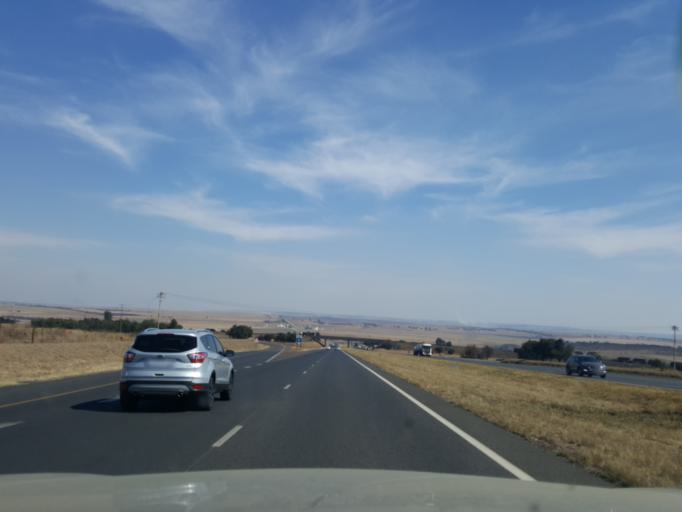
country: ZA
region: Mpumalanga
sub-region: Nkangala District Municipality
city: Middelburg
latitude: -25.8419
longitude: 29.4089
